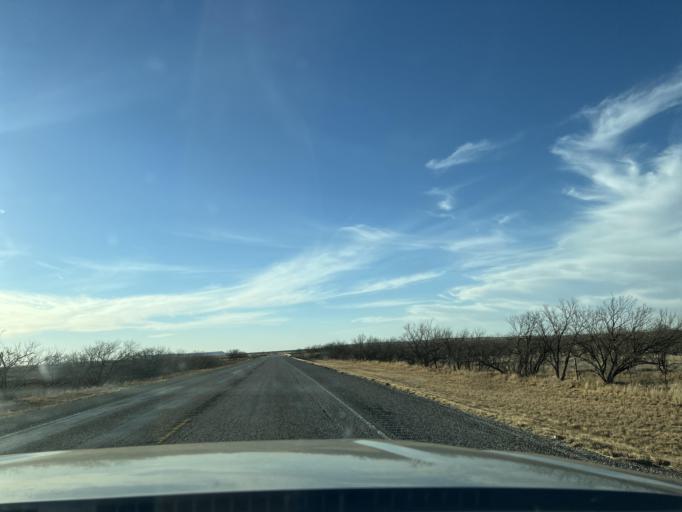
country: US
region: Texas
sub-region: Borden County
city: Gail
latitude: 32.7698
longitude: -101.3251
